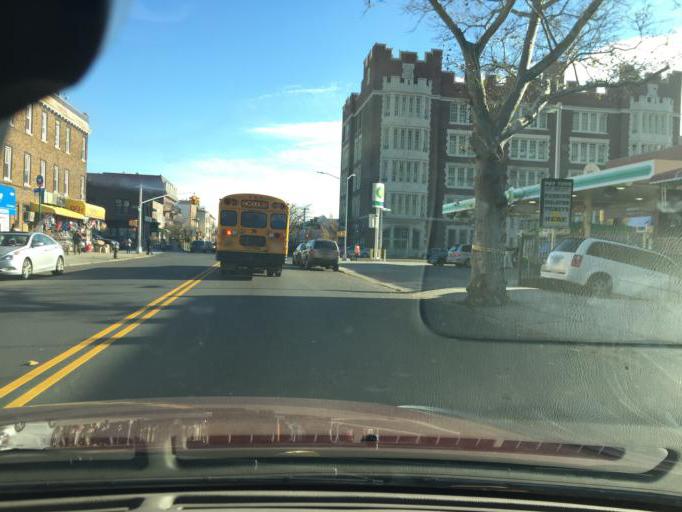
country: US
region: New York
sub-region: Kings County
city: Bensonhurst
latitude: 40.6224
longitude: -73.9880
